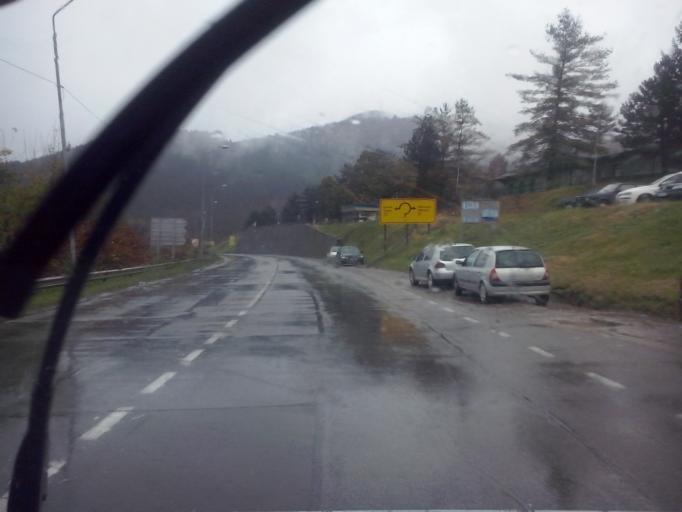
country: RS
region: Central Serbia
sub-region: Raski Okrug
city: Raska
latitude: 43.2844
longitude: 20.6188
